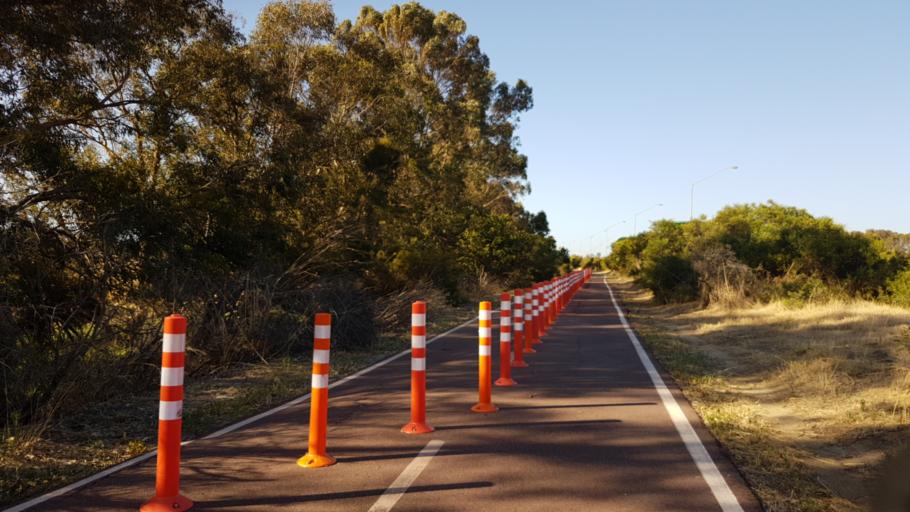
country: AU
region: Western Australia
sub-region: Kwinana
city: Wellard
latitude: -32.2995
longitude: 115.8337
